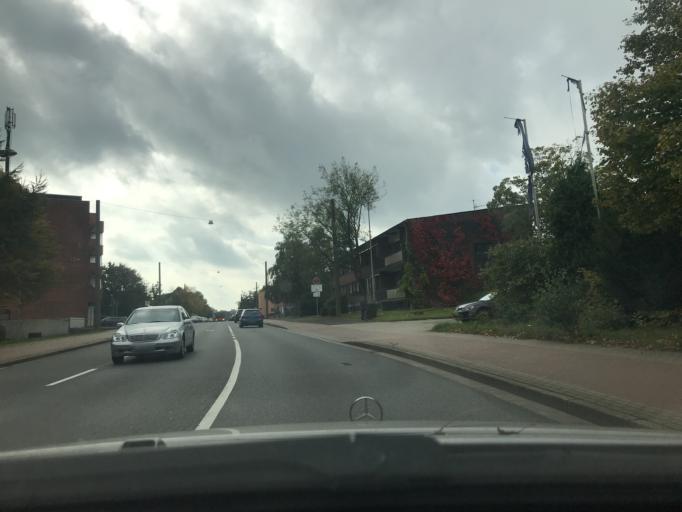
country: DE
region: North Rhine-Westphalia
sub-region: Regierungsbezirk Dusseldorf
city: Moers
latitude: 51.4615
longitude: 6.6305
